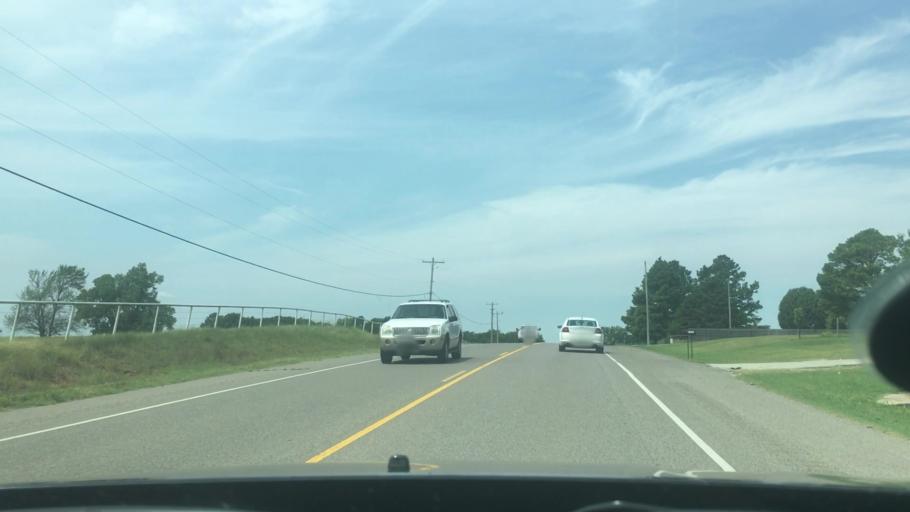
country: US
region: Oklahoma
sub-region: Pottawatomie County
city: Shawnee
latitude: 35.3331
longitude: -96.8203
